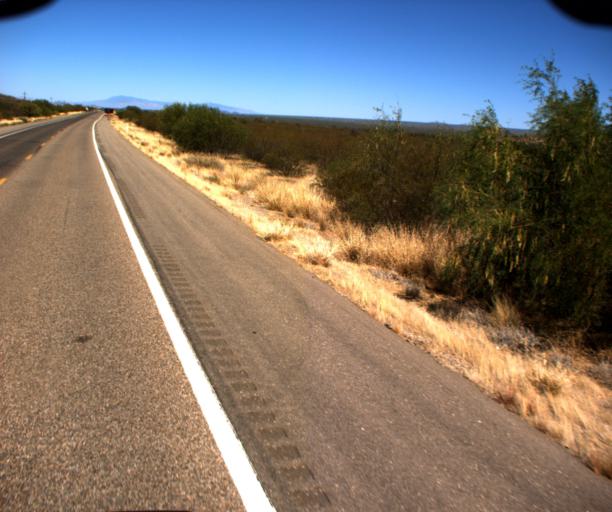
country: US
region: Arizona
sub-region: Pima County
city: Three Points
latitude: 32.0613
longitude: -111.3917
